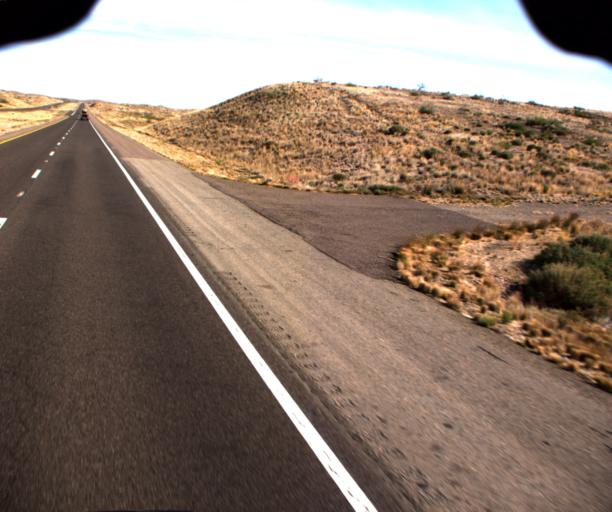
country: US
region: Arizona
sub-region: Cochise County
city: Willcox
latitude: 32.4136
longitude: -109.6620
